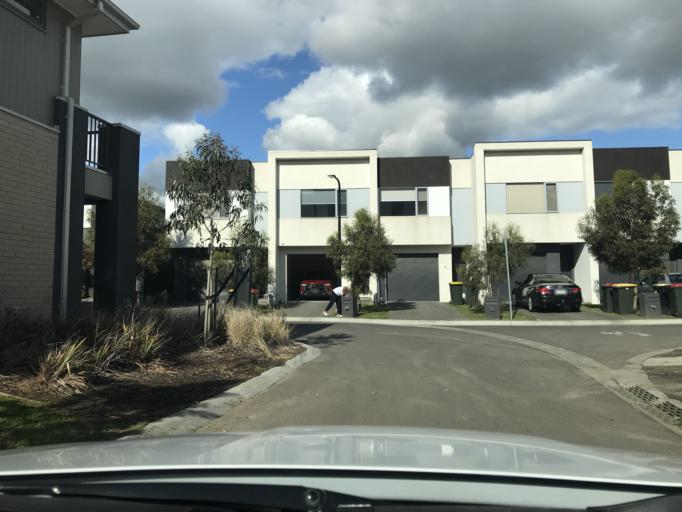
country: AU
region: Victoria
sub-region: Hume
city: Roxburgh Park
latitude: -37.5905
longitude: 144.9022
